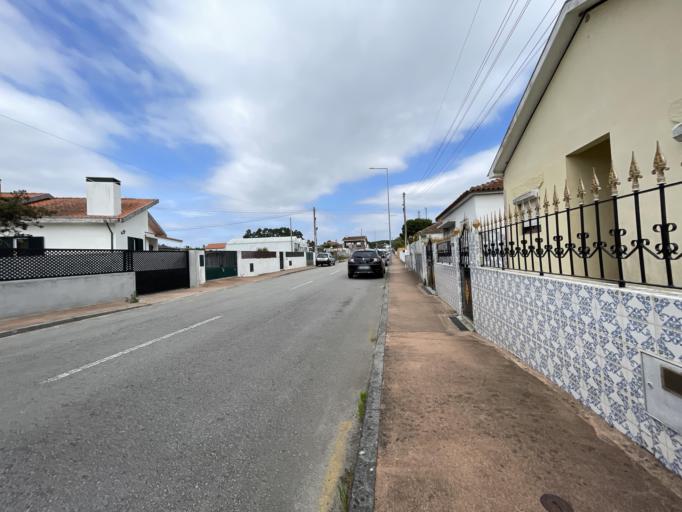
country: PT
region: Aveiro
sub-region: Ovar
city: Cortegaca
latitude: 40.9413
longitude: -8.6332
